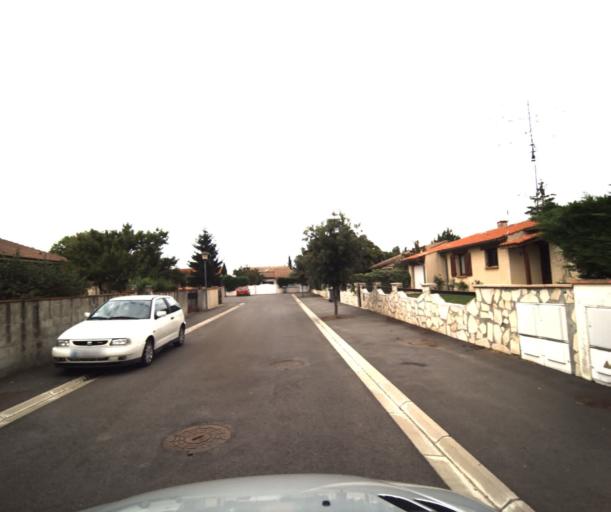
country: FR
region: Midi-Pyrenees
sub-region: Departement de la Haute-Garonne
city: Labarthe-sur-Leze
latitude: 43.4463
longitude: 1.3984
